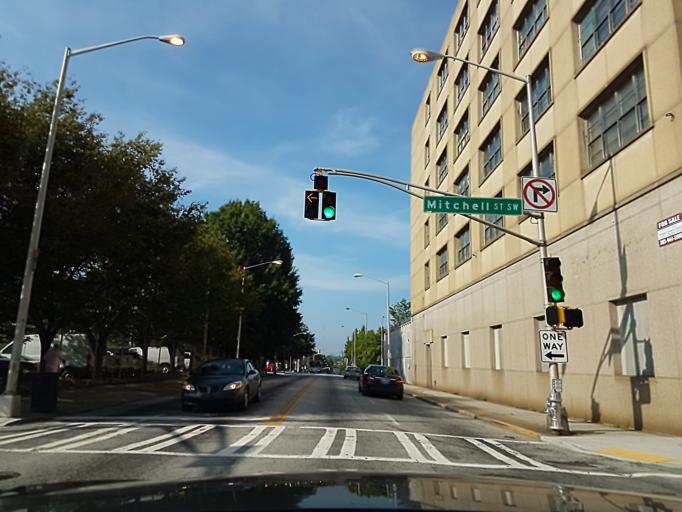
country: US
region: Georgia
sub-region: Fulton County
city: Atlanta
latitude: 33.7517
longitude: -84.3943
